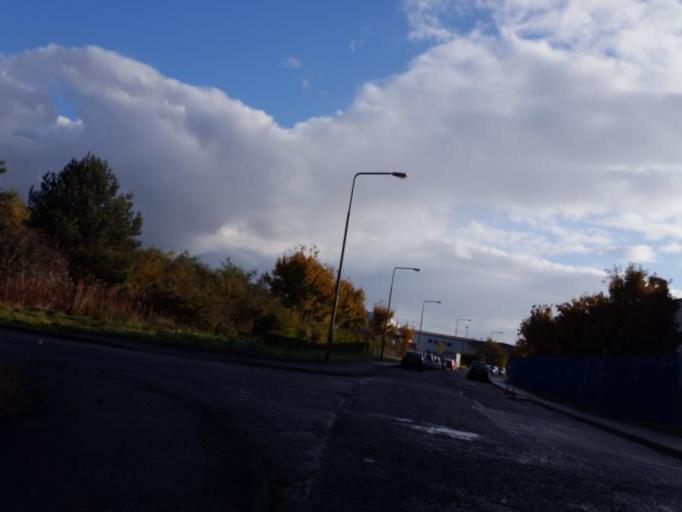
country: GB
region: Scotland
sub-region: West Lothian
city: West Calder
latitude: 55.8929
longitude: -3.5774
